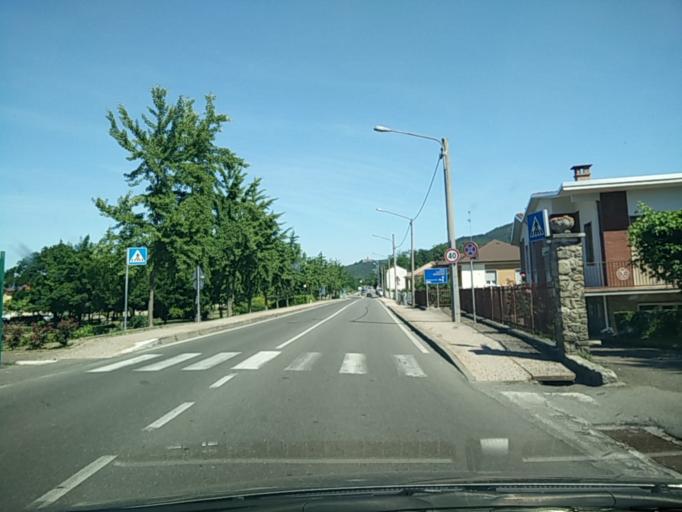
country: IT
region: Lombardy
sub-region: Provincia di Pavia
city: Godiasco
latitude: 44.8971
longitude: 9.0548
